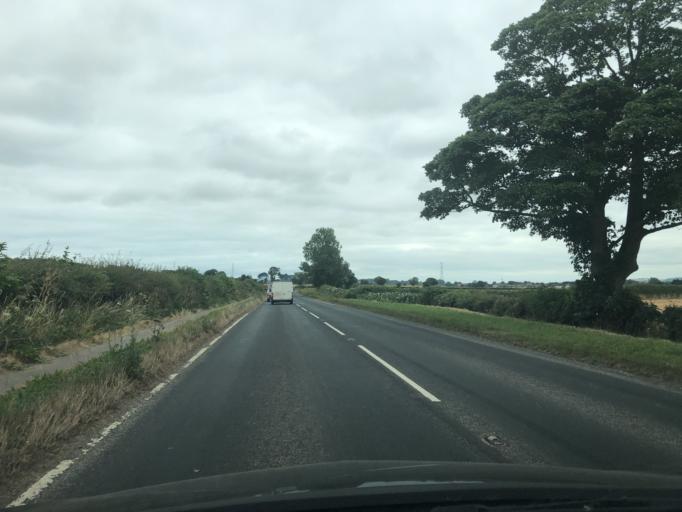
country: GB
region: England
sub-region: North Yorkshire
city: East Ayton
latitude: 54.2496
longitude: -0.4653
